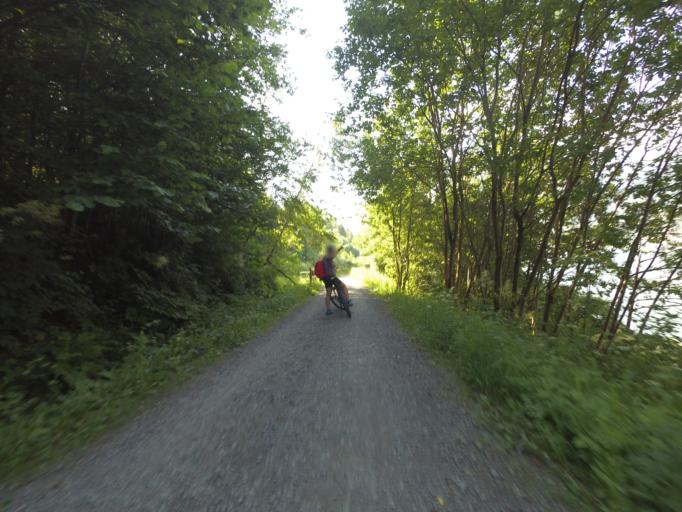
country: AT
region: Carinthia
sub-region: Politischer Bezirk Spittal an der Drau
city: Millstatt
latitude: 46.7913
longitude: 13.5752
